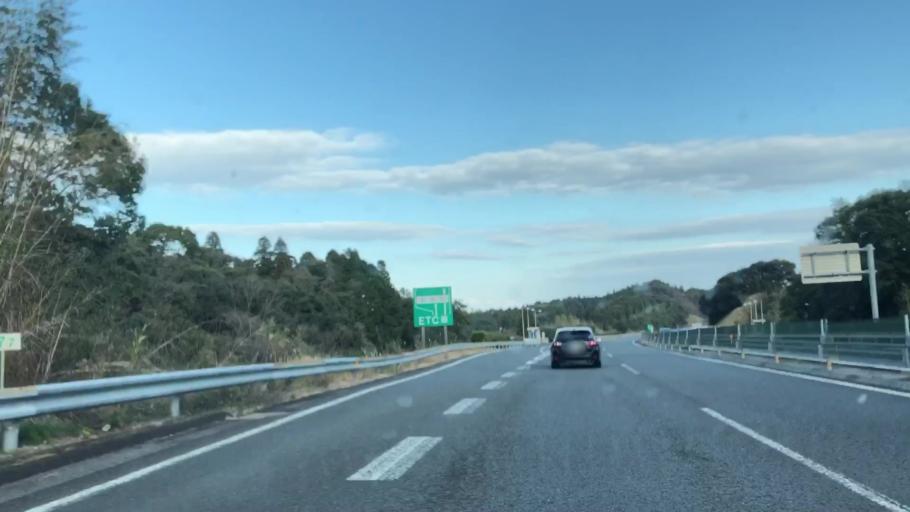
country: JP
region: Miyazaki
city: Miyazaki-shi
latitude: 31.8663
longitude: 131.3874
